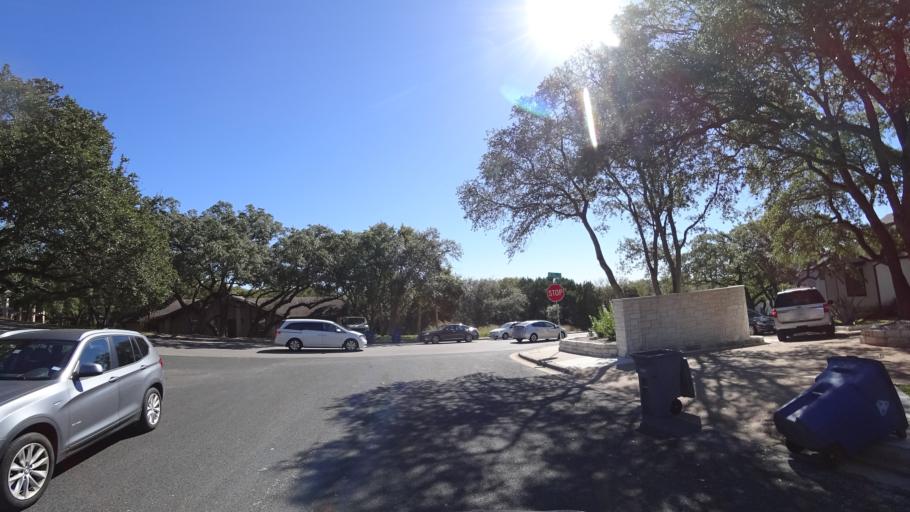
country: US
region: Texas
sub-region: Travis County
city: West Lake Hills
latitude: 30.3489
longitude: -97.7723
